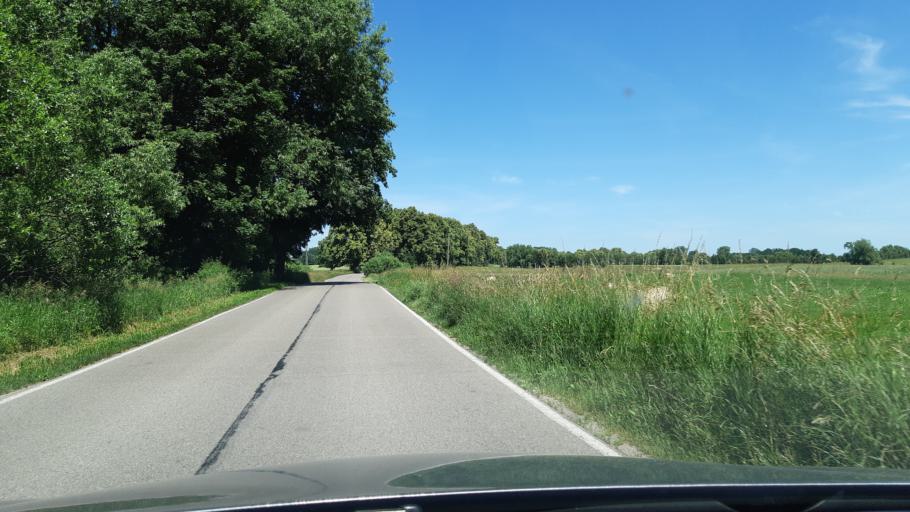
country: PL
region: Warmian-Masurian Voivodeship
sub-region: Powiat gizycki
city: Ryn
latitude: 53.9087
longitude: 21.6745
